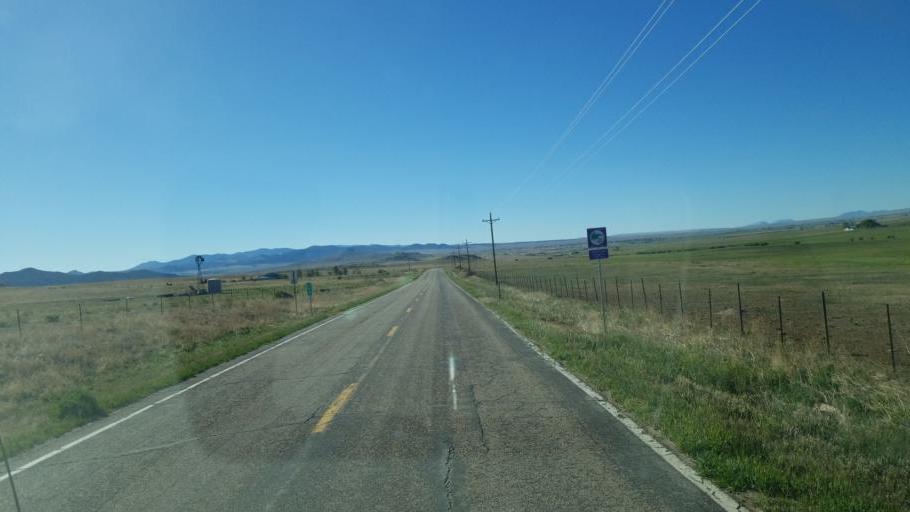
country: US
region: Colorado
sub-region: Custer County
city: Westcliffe
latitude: 38.1919
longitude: -105.5221
